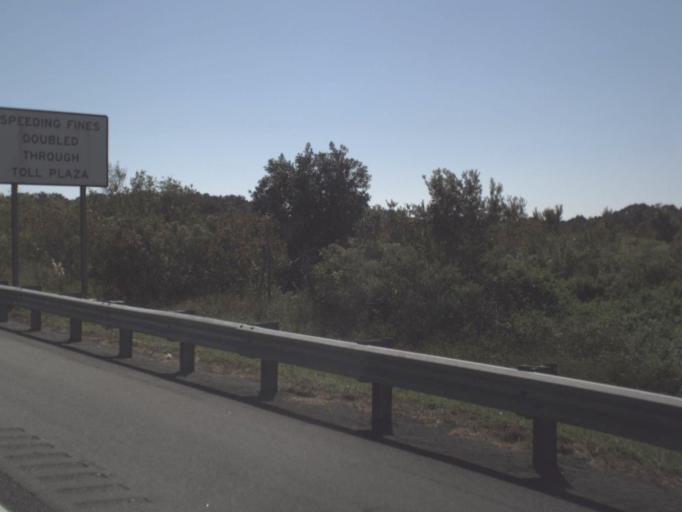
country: US
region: Florida
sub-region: Lake County
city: Yalaha
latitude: 28.6833
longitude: -81.8629
